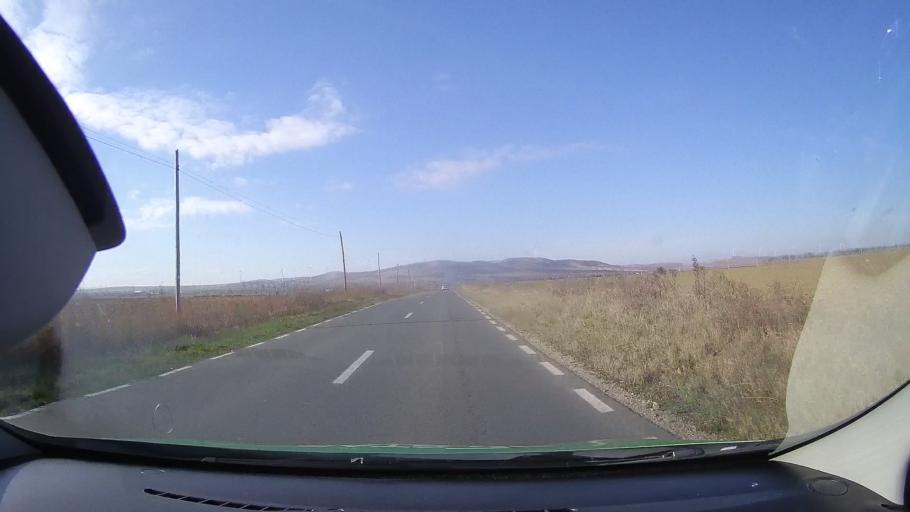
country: RO
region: Tulcea
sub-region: Comuna Valea Nucarilor
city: Valea Nucarilor
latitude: 45.0374
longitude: 28.9059
